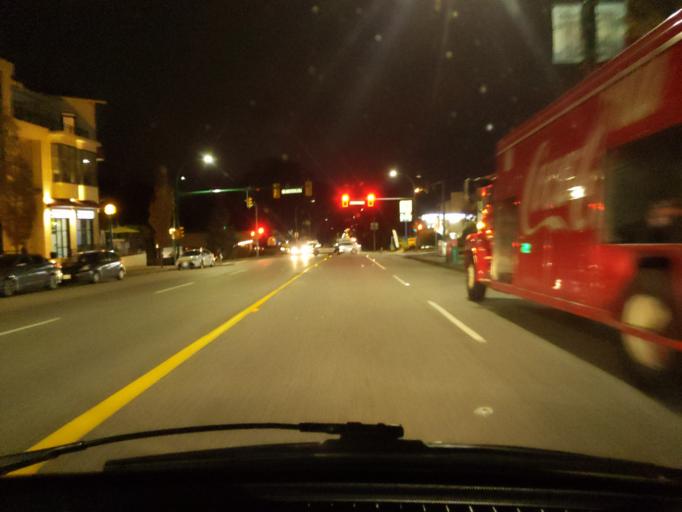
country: CA
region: British Columbia
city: Burnaby
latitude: 49.2547
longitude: -123.0207
